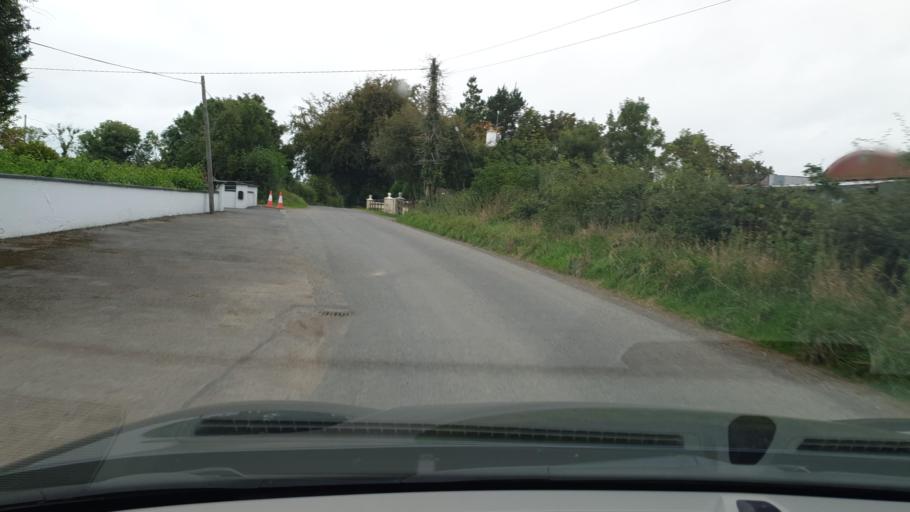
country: IE
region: Leinster
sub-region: An Mhi
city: Dunshaughlin
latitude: 53.5568
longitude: -6.5152
